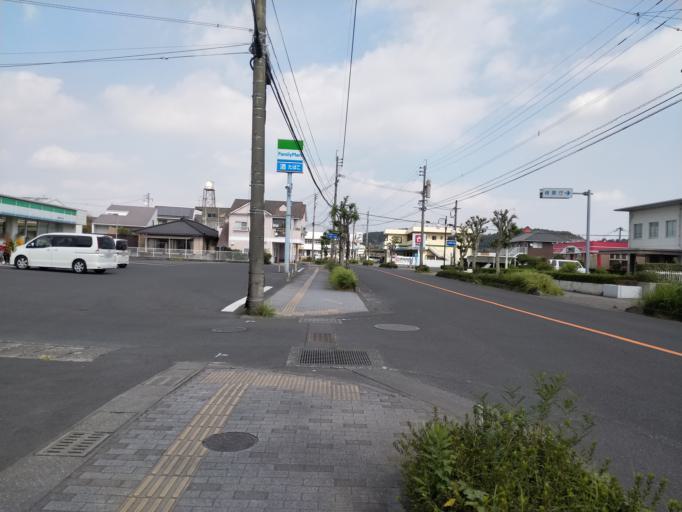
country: JP
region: Kagoshima
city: Kanoya
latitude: 31.3930
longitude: 130.8534
